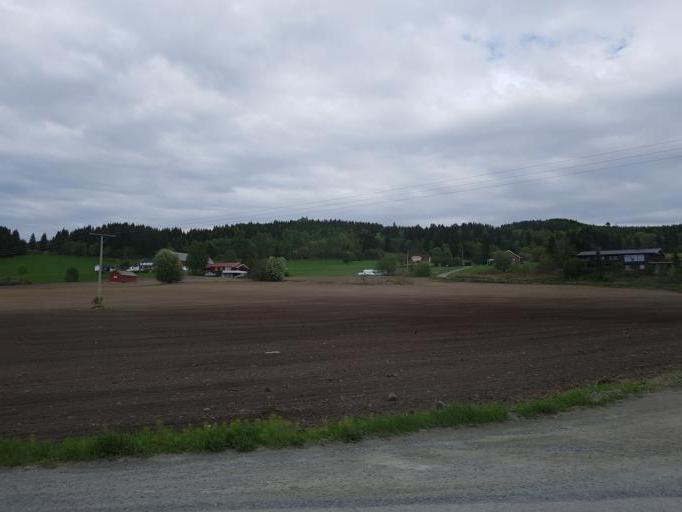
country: NO
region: Nord-Trondelag
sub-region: Levanger
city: Skogn
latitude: 63.7122
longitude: 11.2504
